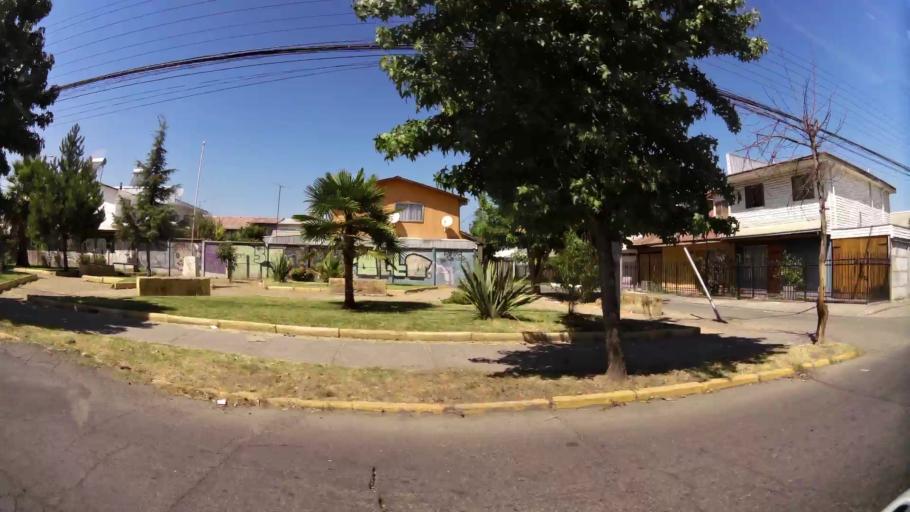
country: CL
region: Maule
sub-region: Provincia de Curico
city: Curico
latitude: -34.9703
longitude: -71.2355
